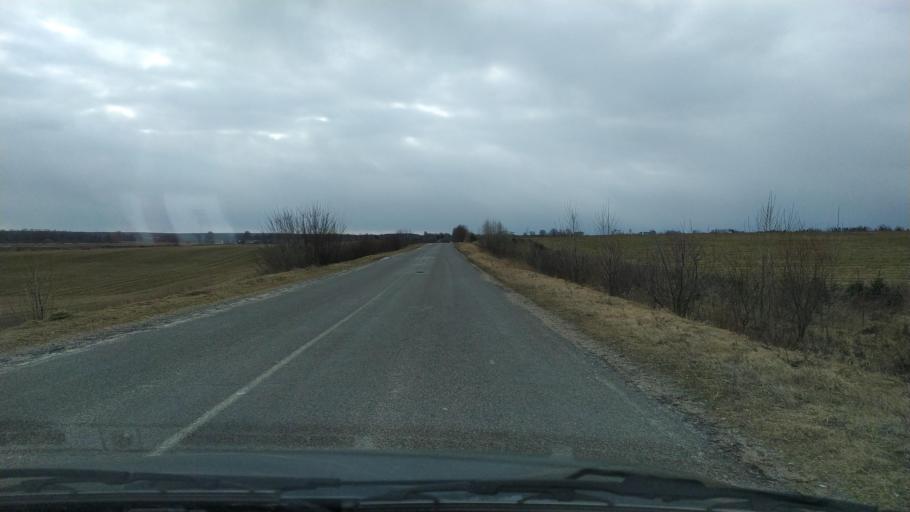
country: BY
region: Brest
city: Kamyanyets
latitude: 52.4169
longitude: 23.8038
